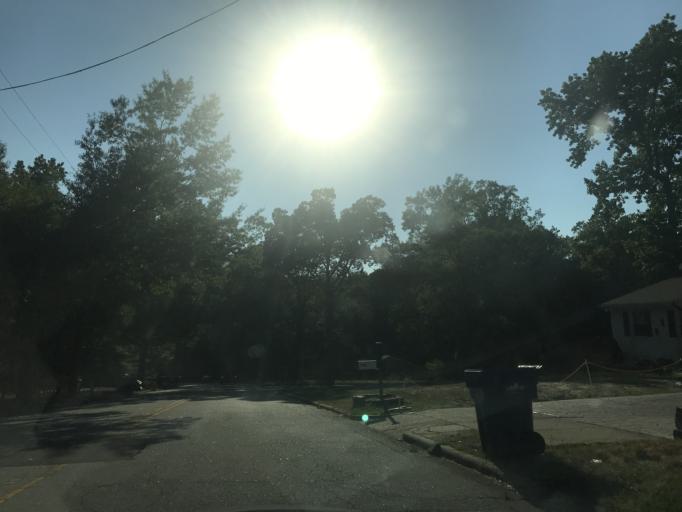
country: US
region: North Carolina
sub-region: Wake County
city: Garner
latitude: 35.7420
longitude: -78.6182
